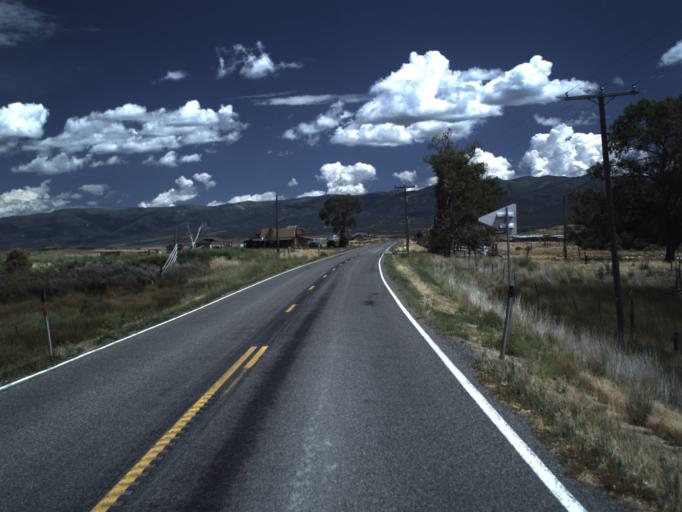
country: US
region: Utah
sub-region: Sanpete County
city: Moroni
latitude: 39.4786
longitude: -111.5459
